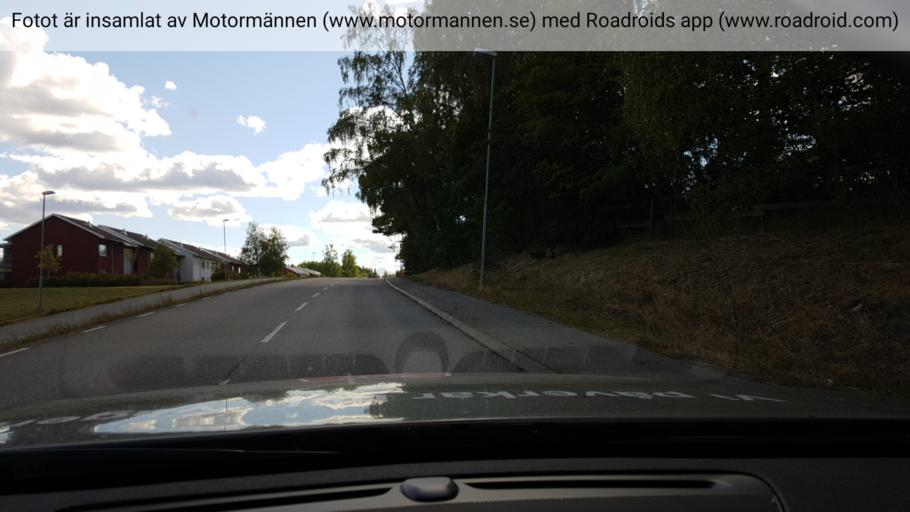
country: SE
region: Stockholm
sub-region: Sigtuna Kommun
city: Sigtuna
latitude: 59.6269
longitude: 17.7575
